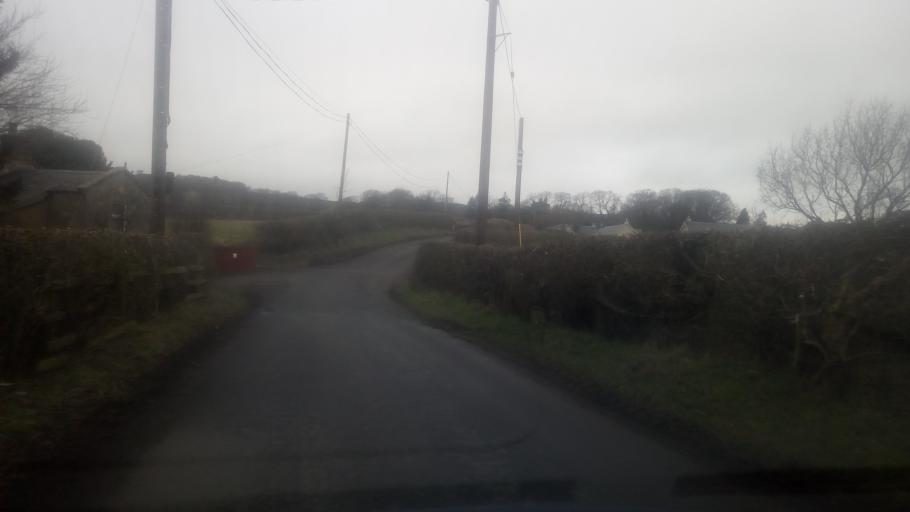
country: GB
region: Scotland
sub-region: The Scottish Borders
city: Jedburgh
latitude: 55.5221
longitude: -2.5172
